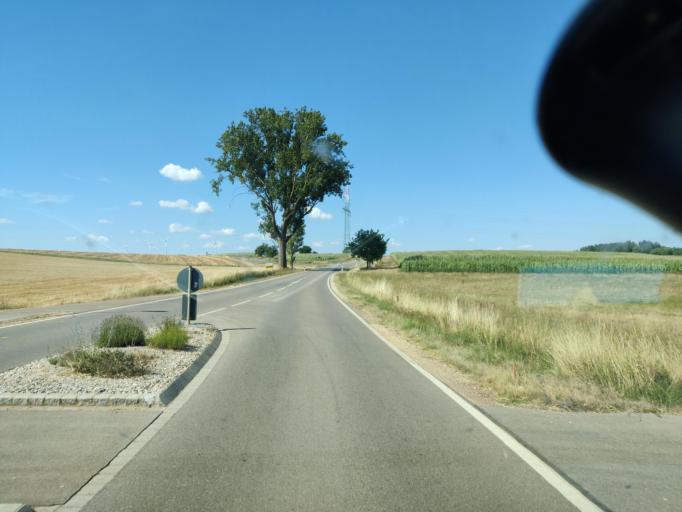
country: DE
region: Bavaria
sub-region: Regierungsbezirk Mittelfranken
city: Bergen
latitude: 49.0734
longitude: 11.1089
